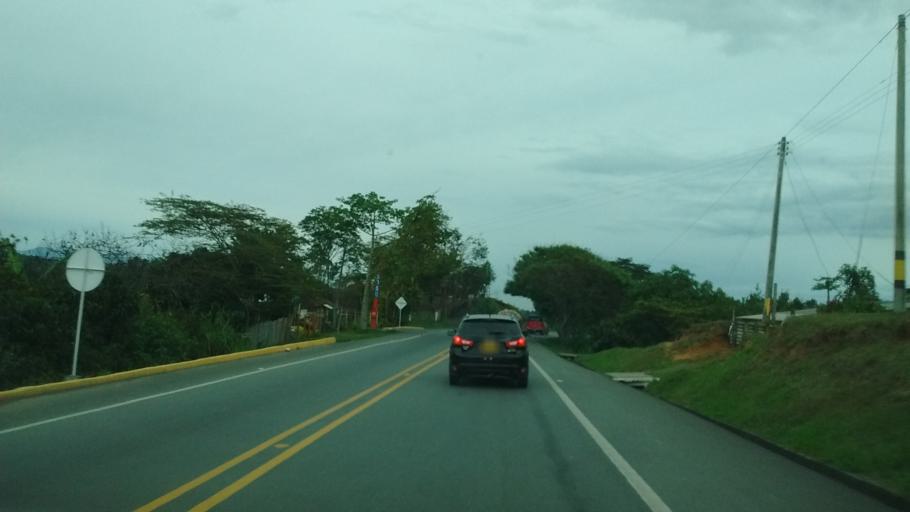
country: CO
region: Cauca
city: Morales
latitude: 2.7771
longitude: -76.5540
